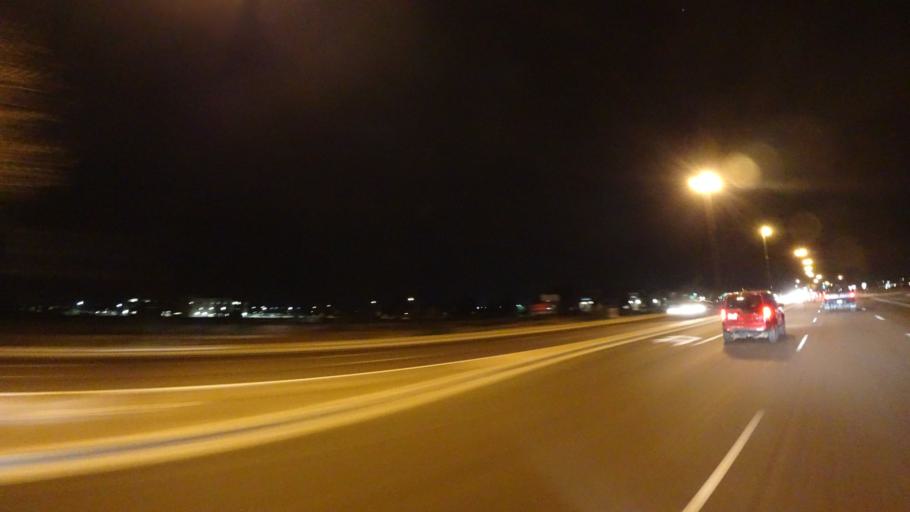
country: US
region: Arizona
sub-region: Maricopa County
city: Gilbert
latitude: 33.2823
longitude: -111.7554
